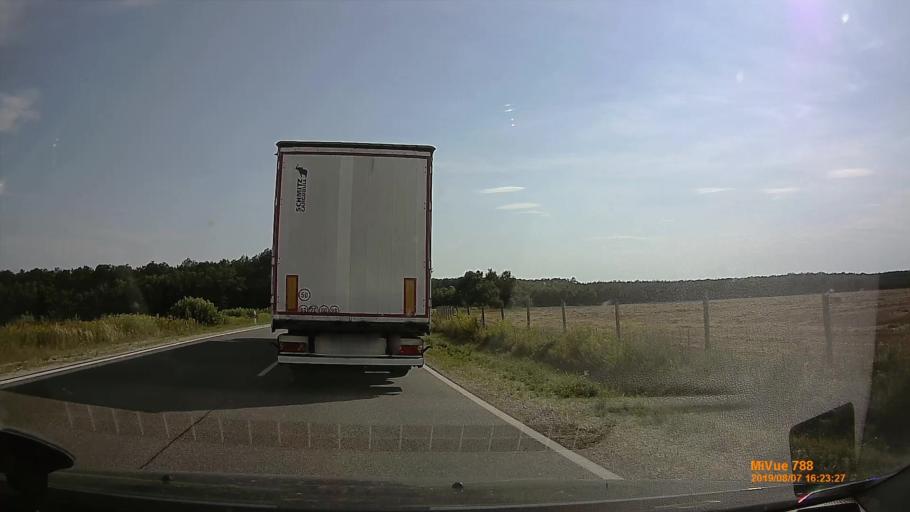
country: HU
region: Zala
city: Zalalovo
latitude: 46.7473
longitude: 16.5568
